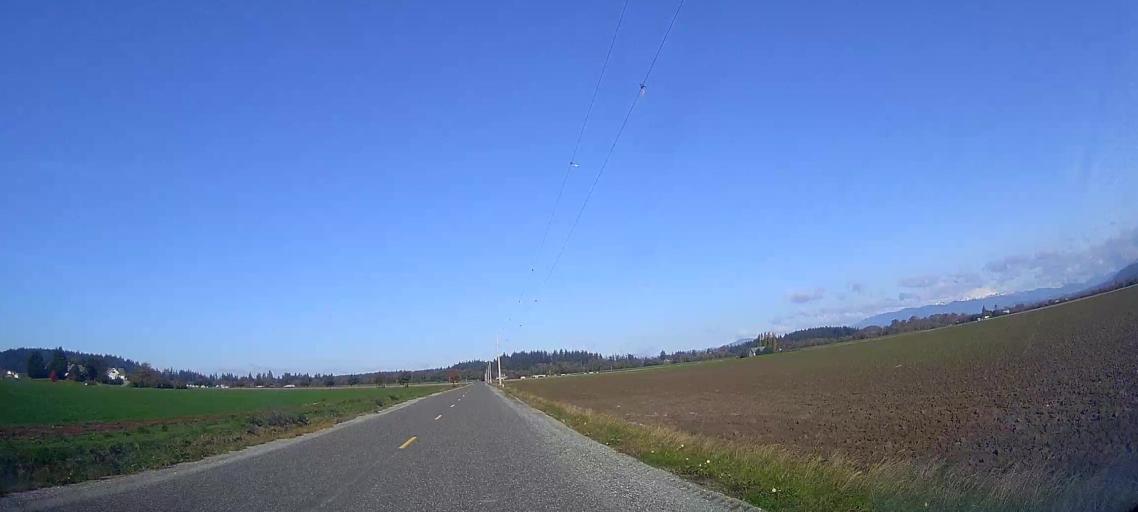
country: US
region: Washington
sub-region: Snohomish County
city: Stanwood
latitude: 48.3459
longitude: -122.4387
